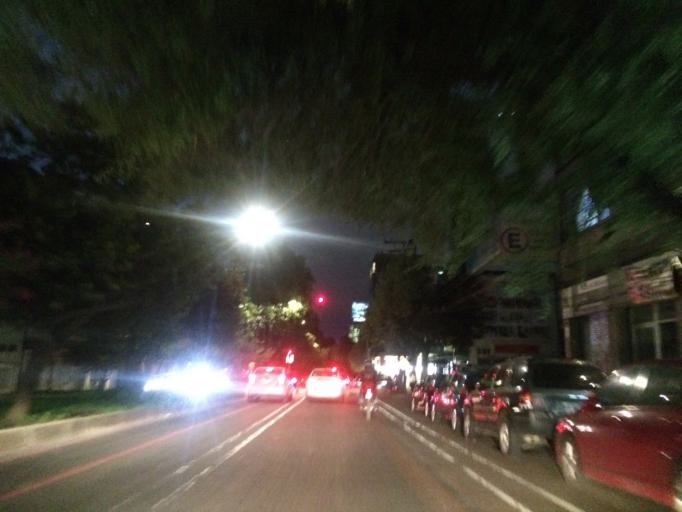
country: MX
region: Mexico City
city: Colonia del Valle
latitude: 19.3941
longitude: -99.1676
